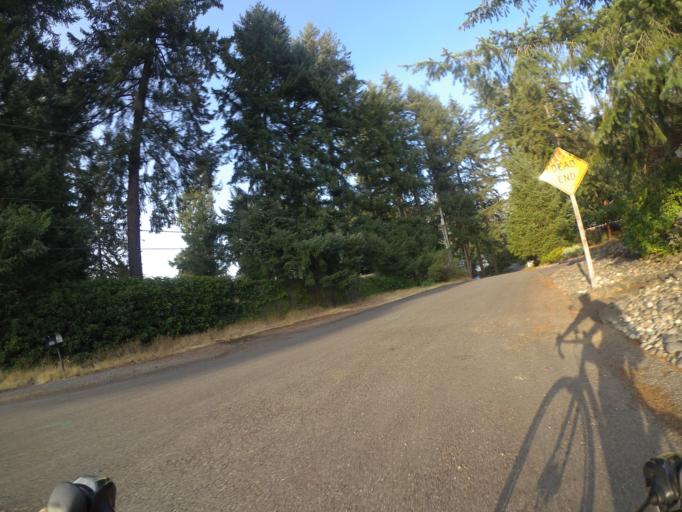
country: US
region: Washington
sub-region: Pierce County
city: Lakewood
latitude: 47.1521
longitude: -122.5185
